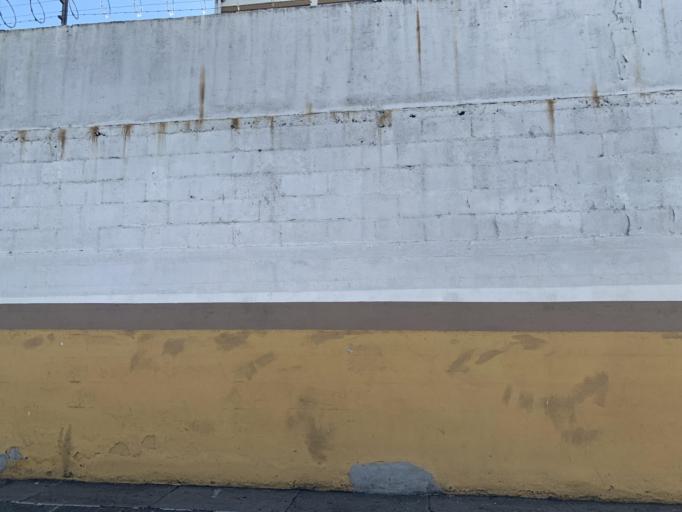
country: GT
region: Guatemala
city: Mixco
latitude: 14.5922
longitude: -90.5615
